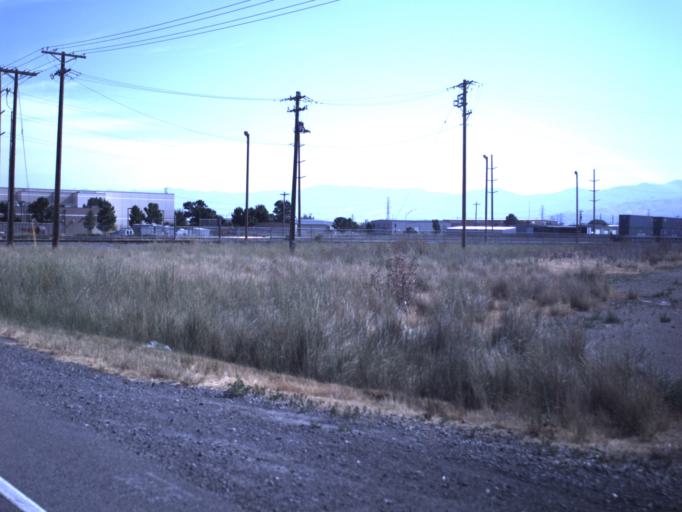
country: US
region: Utah
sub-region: Salt Lake County
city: West Valley City
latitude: 40.7510
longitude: -112.0249
